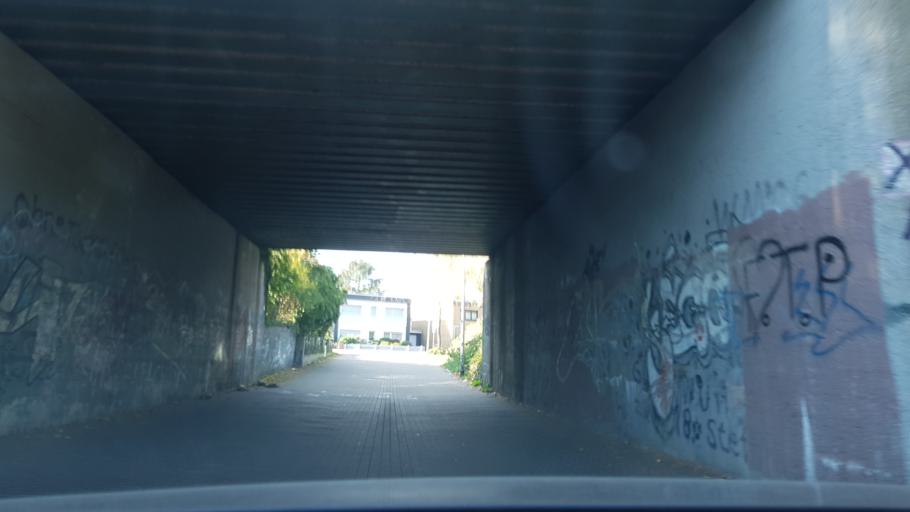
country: DE
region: North Rhine-Westphalia
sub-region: Regierungsbezirk Dusseldorf
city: Moers
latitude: 51.4176
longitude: 6.6736
